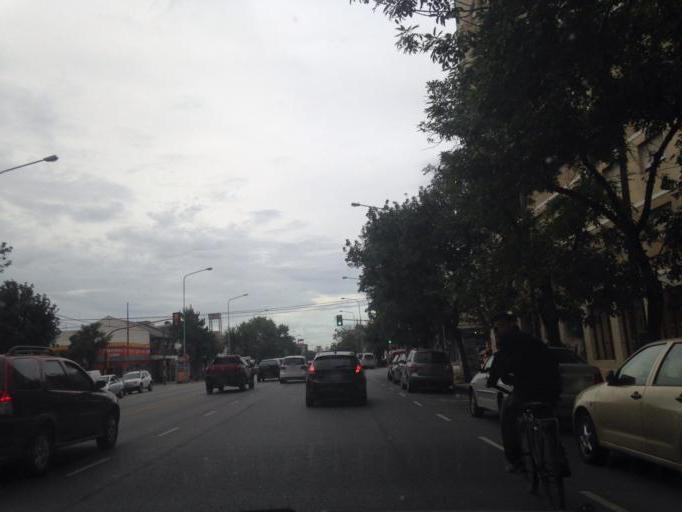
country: AR
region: Buenos Aires
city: Mar del Plata
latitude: -38.0177
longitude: -57.5701
